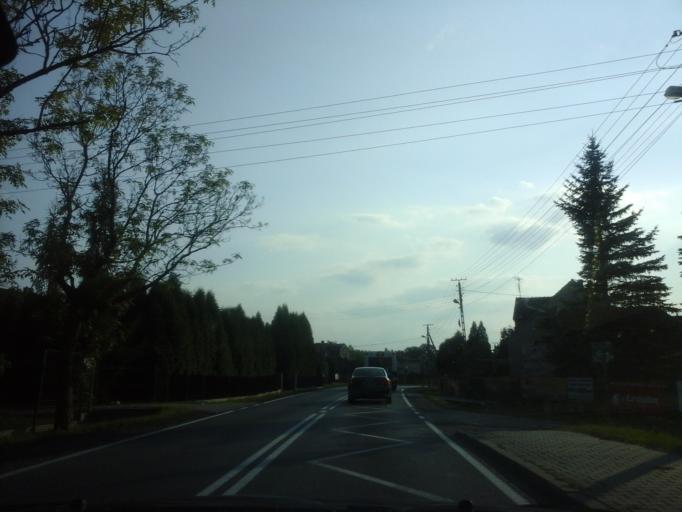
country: PL
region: Lesser Poland Voivodeship
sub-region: Powiat krakowski
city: Rzozow
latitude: 49.9662
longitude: 19.7791
